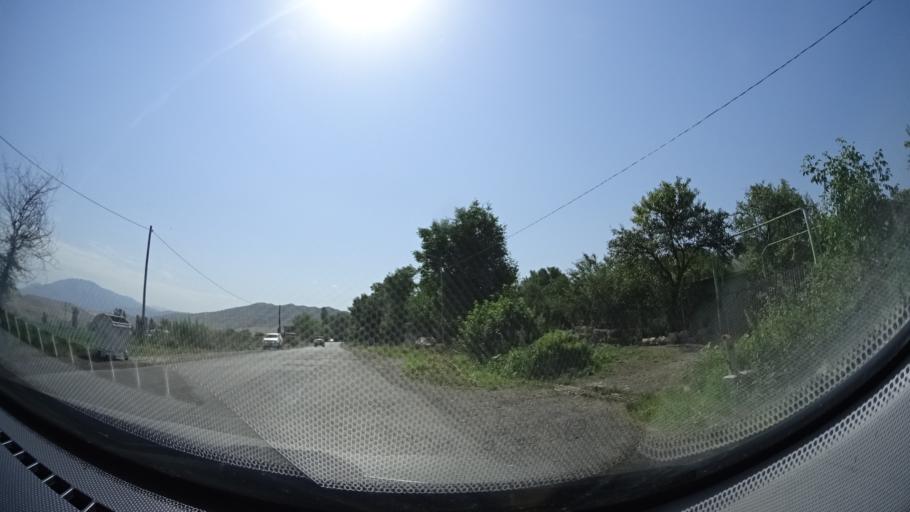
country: GE
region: Samtskhe-Javakheti
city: Akhaltsikhe
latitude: 41.6377
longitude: 43.0356
